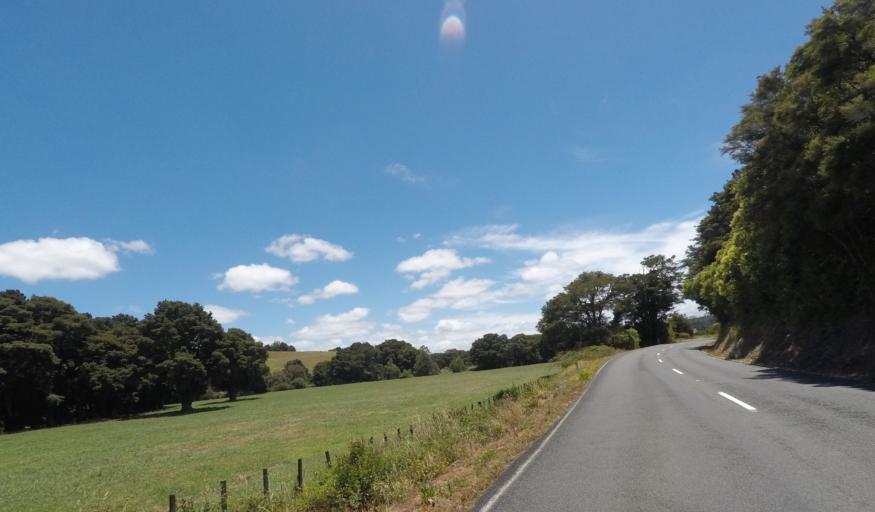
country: NZ
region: Northland
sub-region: Whangarei
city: Whangarei
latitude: -35.5391
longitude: 174.3102
